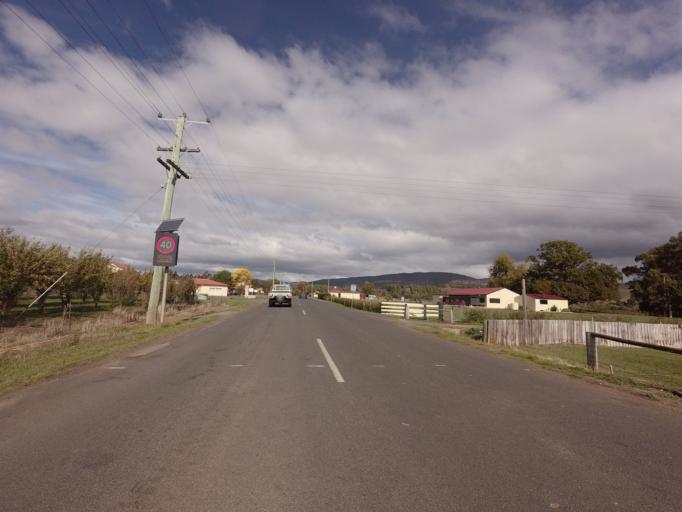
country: AU
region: Tasmania
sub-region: Derwent Valley
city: New Norfolk
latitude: -42.6960
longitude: 146.8881
